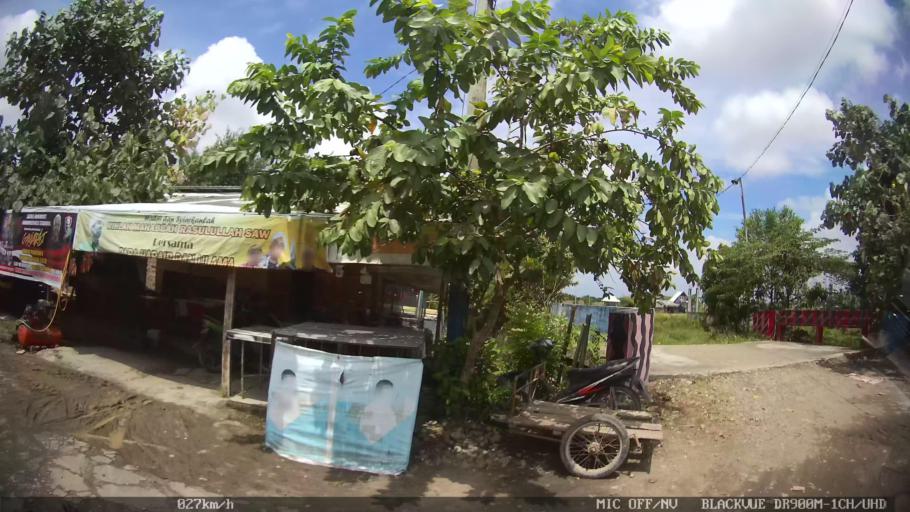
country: ID
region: North Sumatra
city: Percut
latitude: 3.6145
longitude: 98.7815
